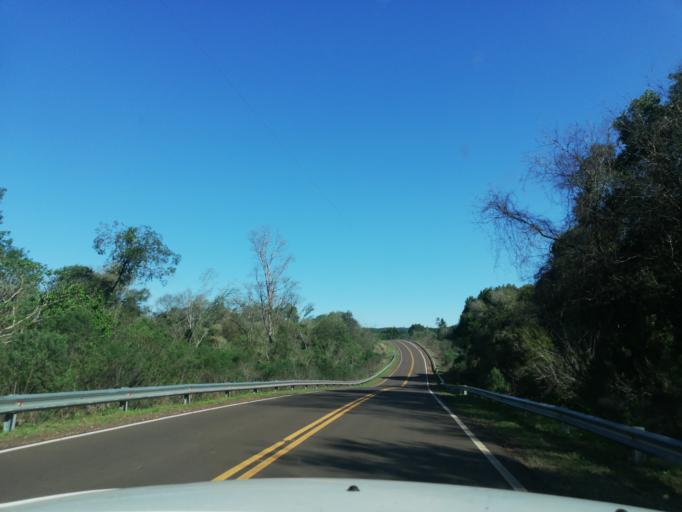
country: AR
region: Misiones
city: Arroyo del Medio
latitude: -27.6800
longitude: -55.3991
